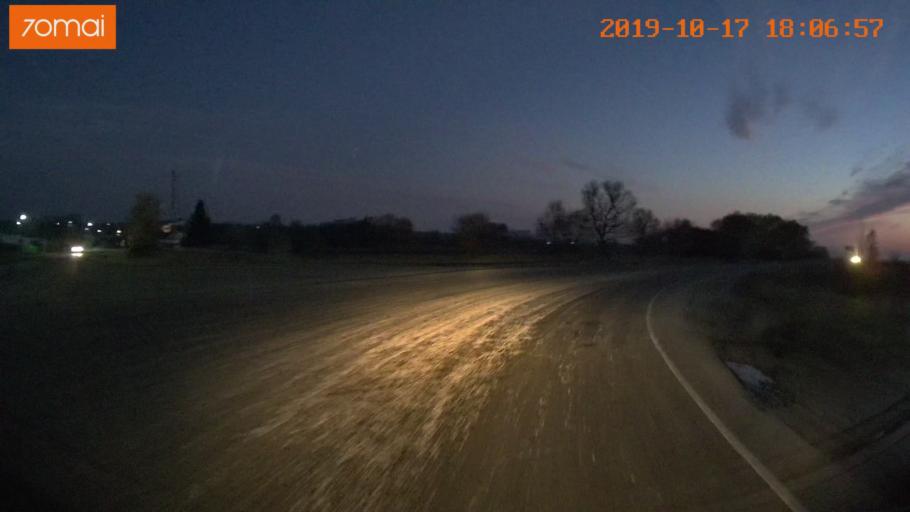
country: RU
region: Tula
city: Kurkino
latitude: 53.4479
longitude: 38.6592
